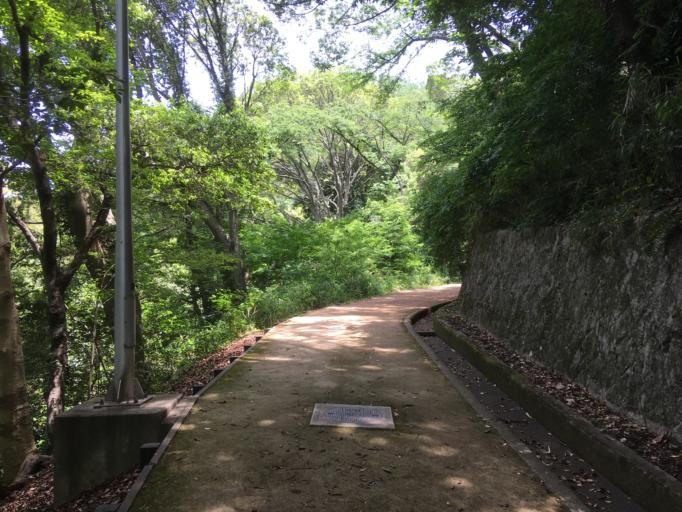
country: JP
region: Nara
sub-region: Ikoma-shi
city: Ikoma
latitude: 34.6716
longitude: 135.6525
